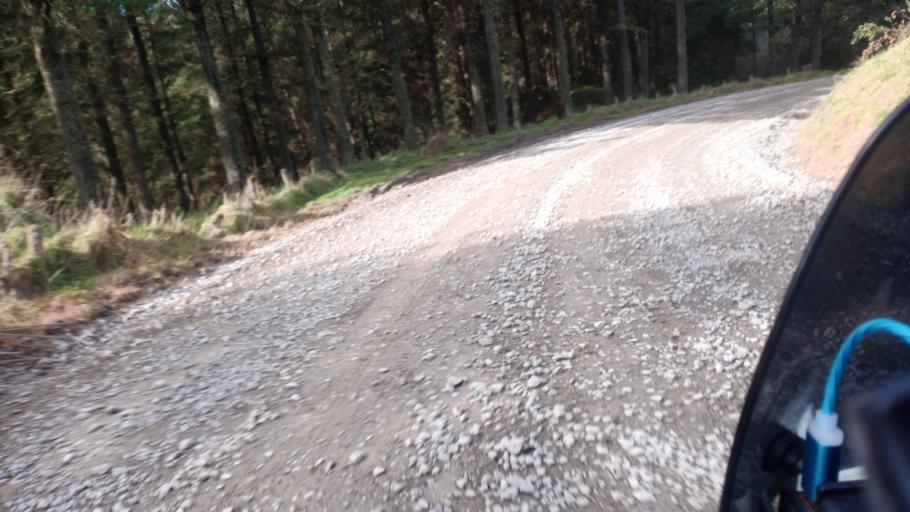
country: NZ
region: Gisborne
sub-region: Gisborne District
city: Gisborne
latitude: -38.1202
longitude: 178.1499
